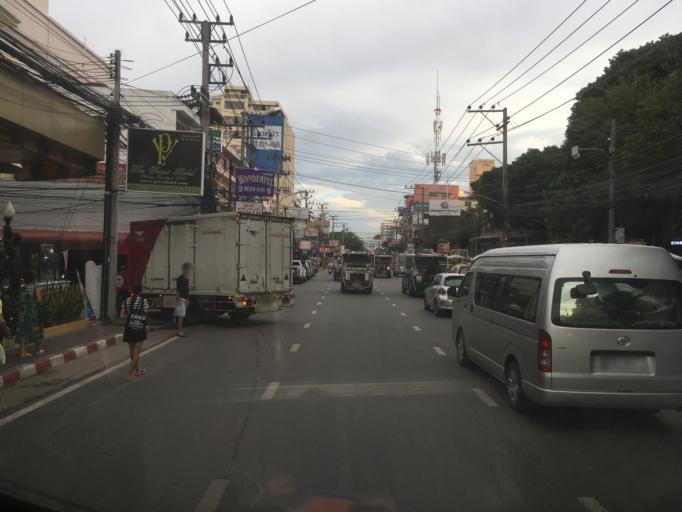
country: TH
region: Chon Buri
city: Phatthaya
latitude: 12.9294
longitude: 100.8803
